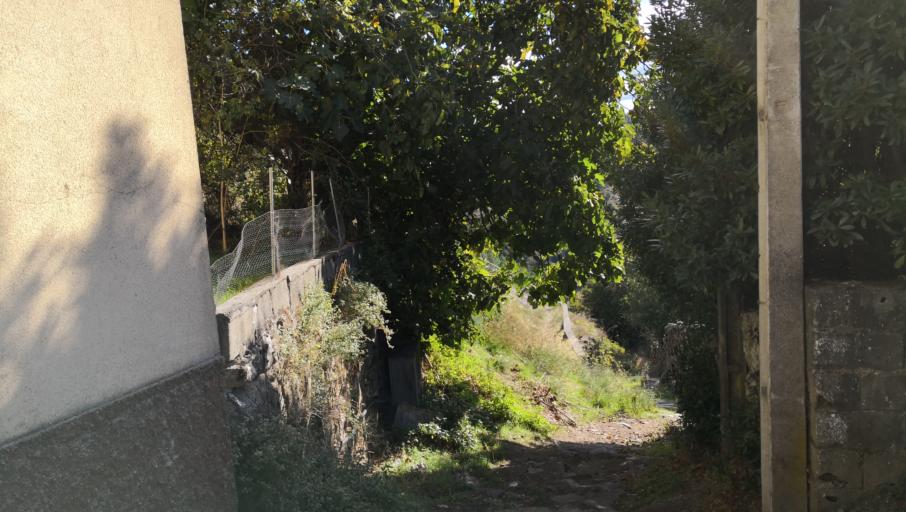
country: PT
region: Vila Real
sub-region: Vila Real
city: Vila Real
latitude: 41.2922
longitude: -7.7477
